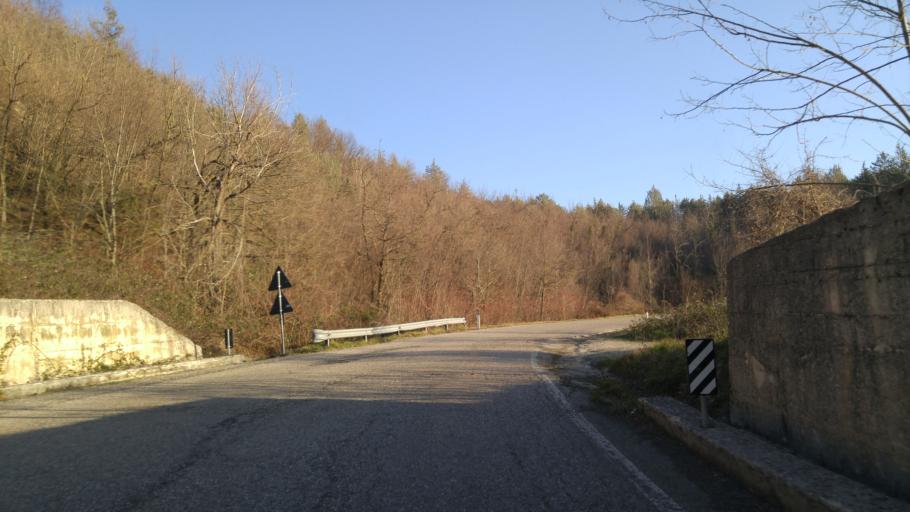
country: IT
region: The Marches
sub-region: Provincia di Pesaro e Urbino
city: Acqualagna
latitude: 43.6550
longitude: 12.6707
